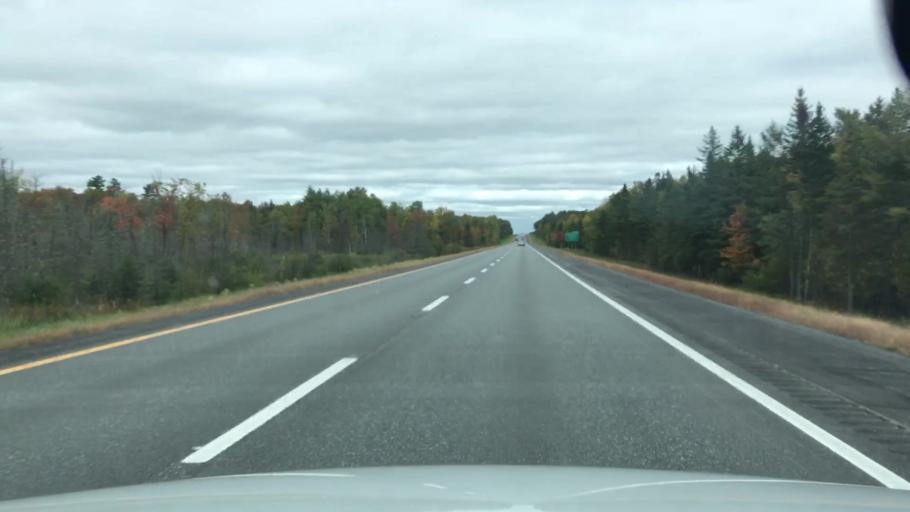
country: US
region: Maine
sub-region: Somerset County
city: Pittsfield
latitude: 44.7518
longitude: -69.4212
